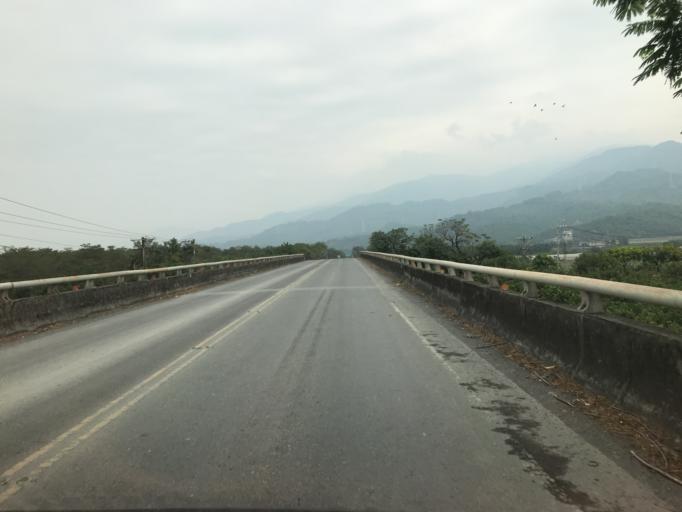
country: TW
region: Taiwan
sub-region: Pingtung
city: Pingtung
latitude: 22.4495
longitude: 120.6079
